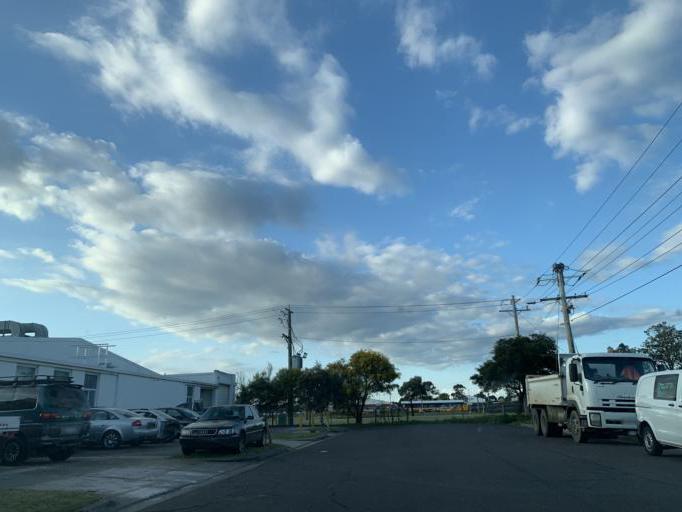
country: AU
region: Victoria
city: Heatherton
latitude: -37.9770
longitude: 145.0887
